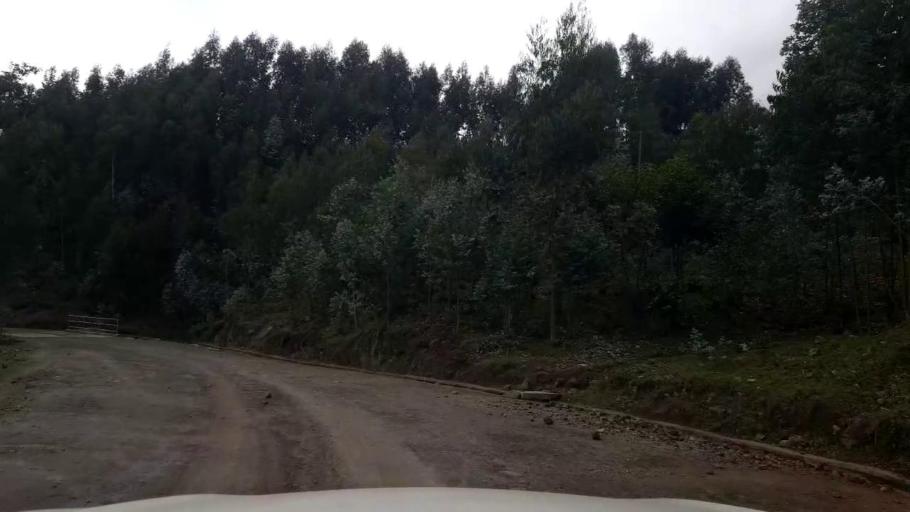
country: RW
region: Northern Province
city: Musanze
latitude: -1.5297
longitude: 29.5307
